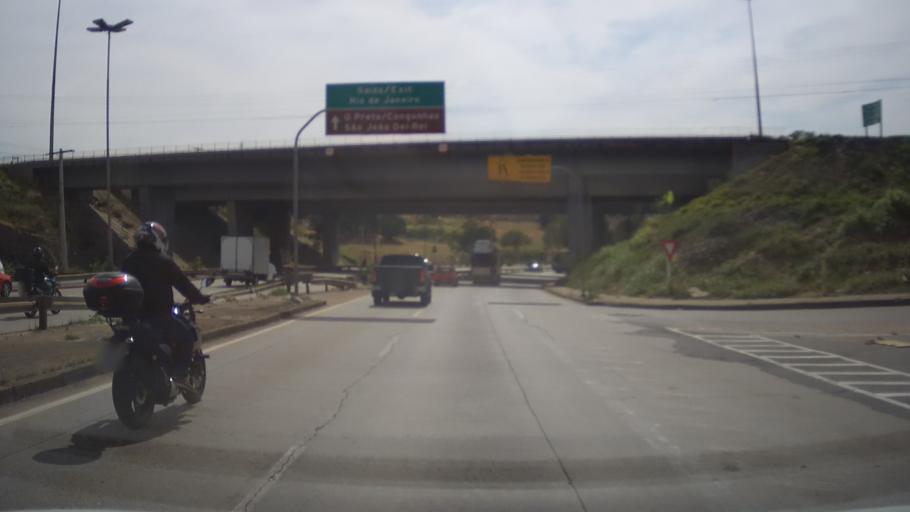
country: BR
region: Minas Gerais
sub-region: Contagem
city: Contagem
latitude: -19.9331
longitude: -44.0084
